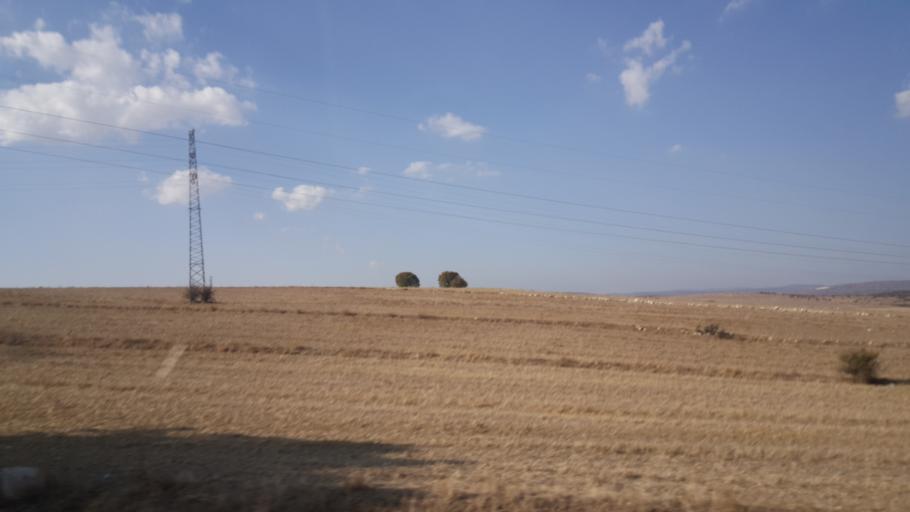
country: TR
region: Eskisehir
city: Kirka
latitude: 39.3188
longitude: 30.5521
